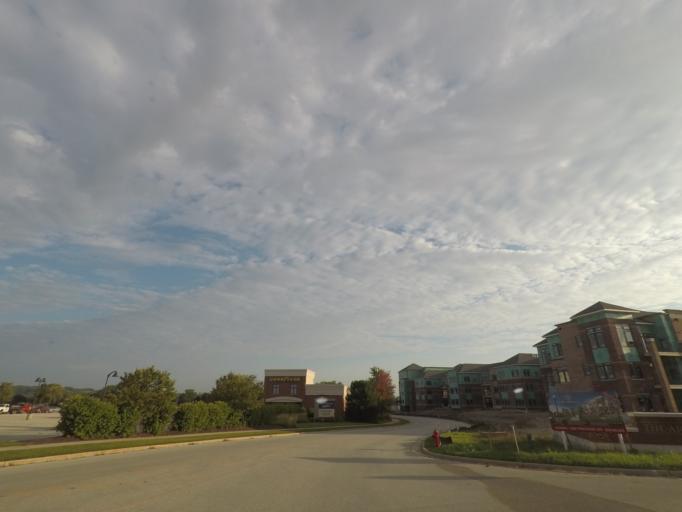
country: US
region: Wisconsin
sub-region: Waukesha County
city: Brookfield
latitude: 43.0373
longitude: -88.1116
